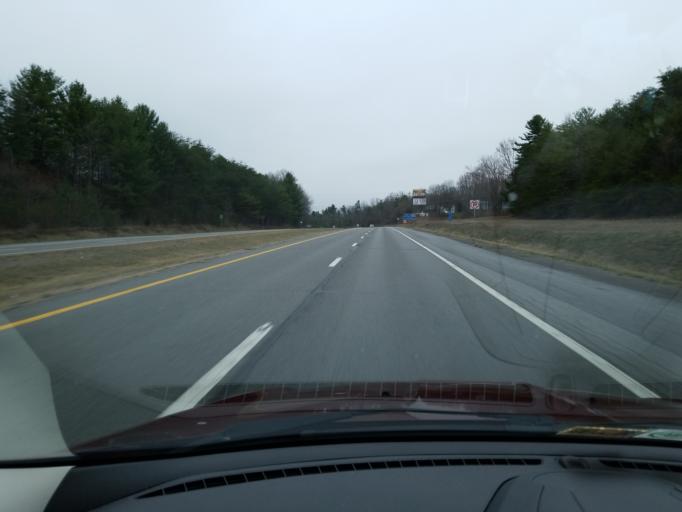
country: US
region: West Virginia
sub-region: Mercer County
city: Athens
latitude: 37.3620
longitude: -81.0297
